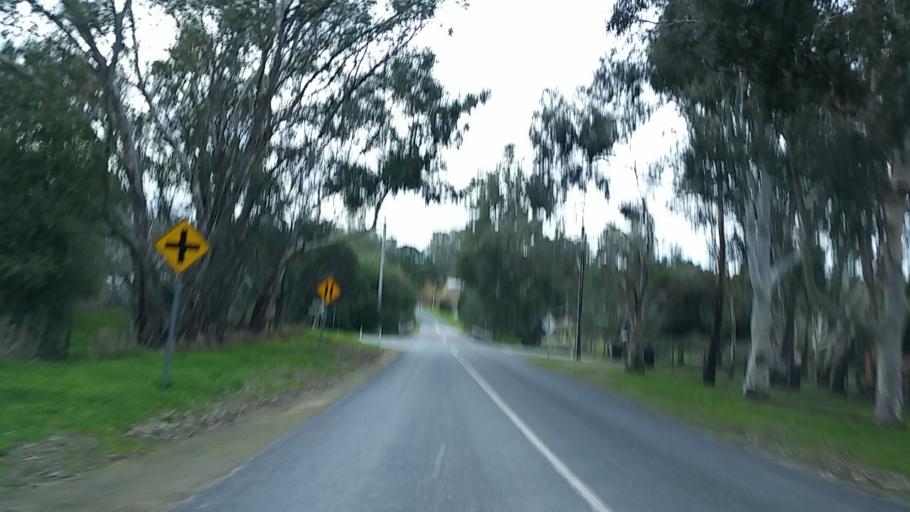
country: AU
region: South Australia
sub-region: Mount Barker
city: Nairne
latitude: -34.9510
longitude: 139.0130
